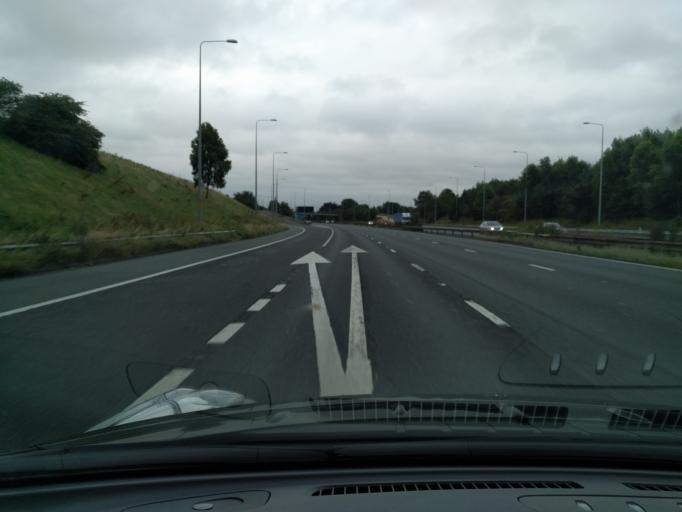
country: GB
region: England
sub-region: St. Helens
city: Newton-le-Willows
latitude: 53.4435
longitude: -2.5876
